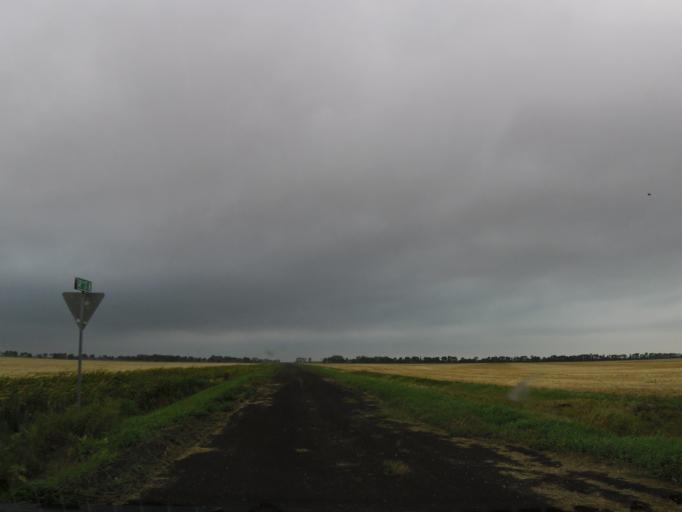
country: US
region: North Dakota
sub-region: Walsh County
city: Grafton
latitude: 48.4850
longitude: -97.1689
